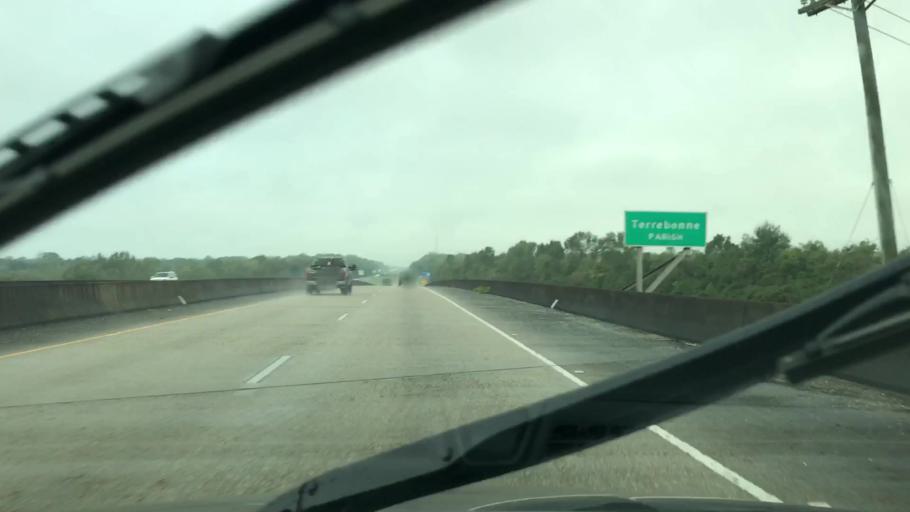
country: US
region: Louisiana
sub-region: Terrebonne Parish
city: Gray
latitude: 29.6827
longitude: -90.7513
